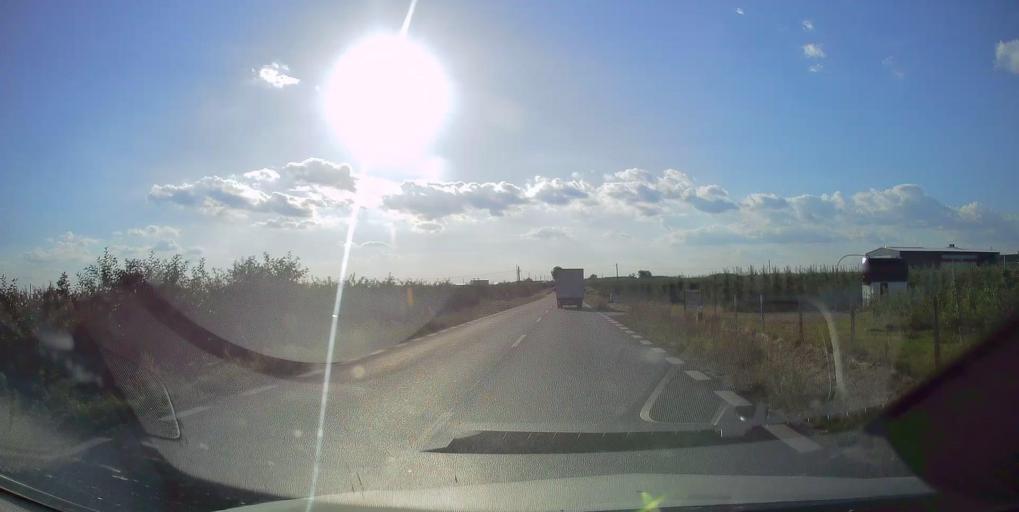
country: PL
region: Lodz Voivodeship
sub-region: Powiat rawski
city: Biala Rawska
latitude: 51.8016
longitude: 20.5104
